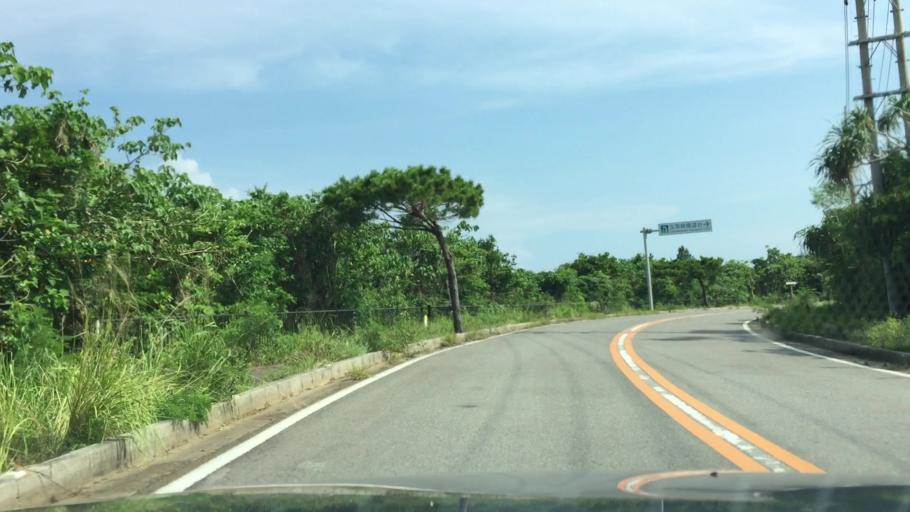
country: JP
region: Okinawa
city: Ishigaki
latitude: 24.4905
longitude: 124.2800
